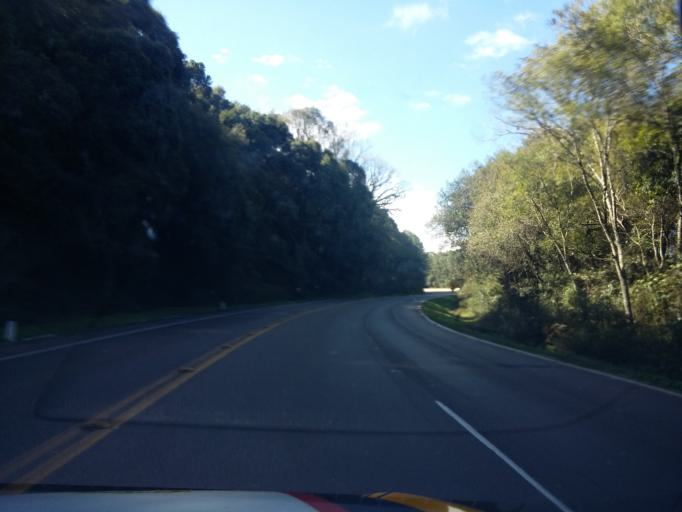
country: BR
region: Rio Grande do Sul
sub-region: Vacaria
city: Vacaria
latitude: -28.5835
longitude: -51.0265
